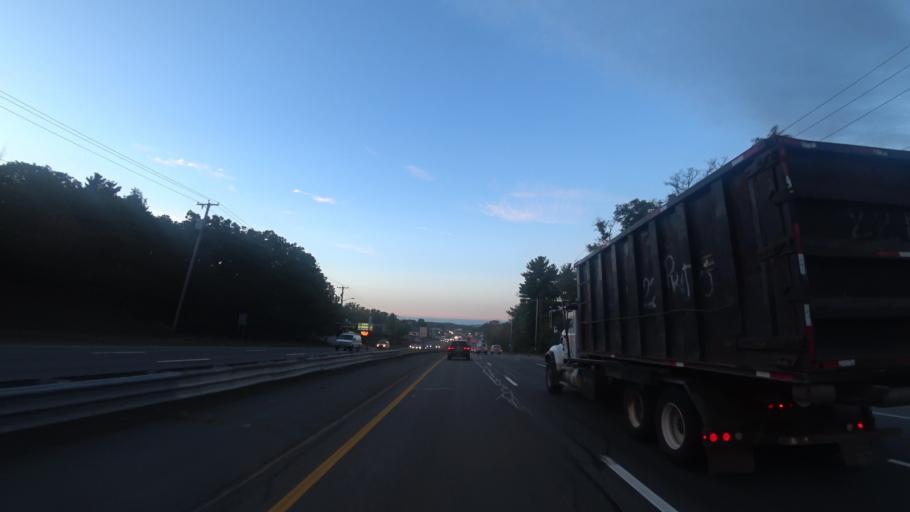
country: US
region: Massachusetts
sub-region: Essex County
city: Saugus
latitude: 42.5019
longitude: -71.0147
